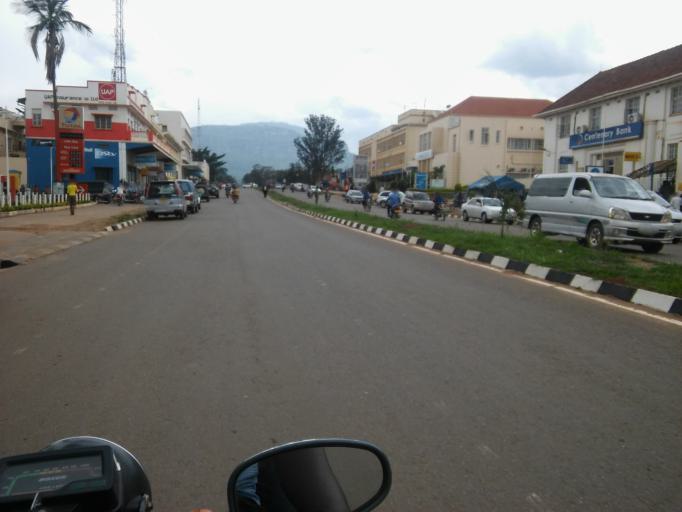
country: UG
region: Eastern Region
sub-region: Mbale District
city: Mbale
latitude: 1.0722
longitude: 34.1809
